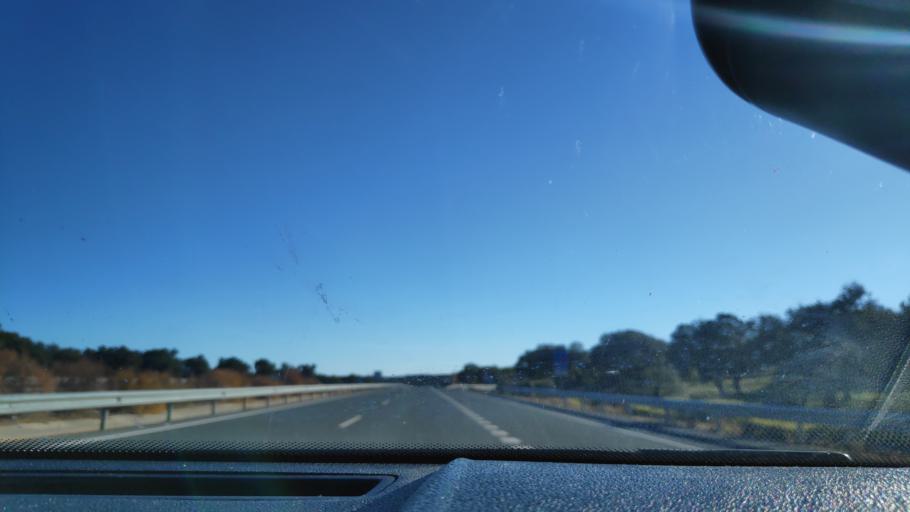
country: ES
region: Andalusia
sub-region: Provincia de Huelva
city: Santa Olalla del Cala
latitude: 37.9502
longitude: -6.2303
